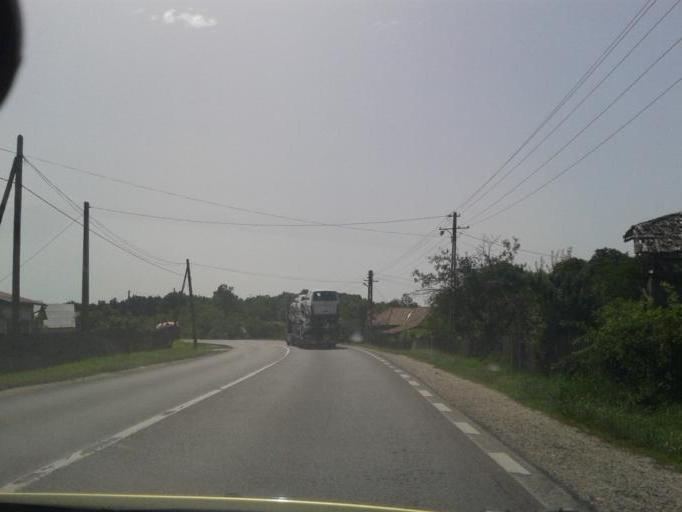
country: RO
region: Arges
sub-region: Comuna Cotmeana
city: Cotmeana
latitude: 44.9826
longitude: 24.6517
